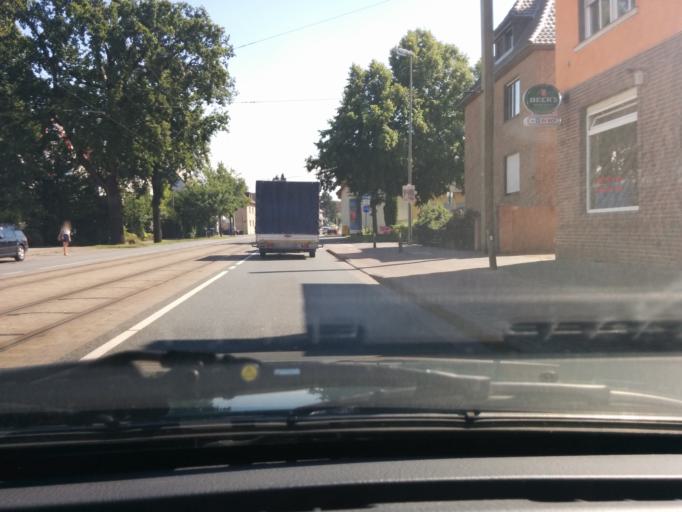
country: DE
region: North Rhine-Westphalia
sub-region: Regierungsbezirk Detmold
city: Bielefeld
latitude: 52.0508
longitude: 8.5208
